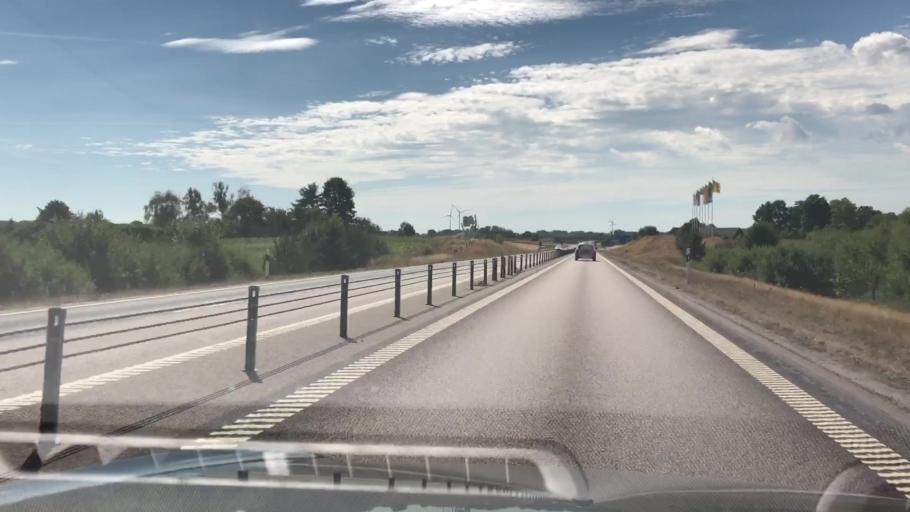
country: SE
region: Kalmar
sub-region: Torsas Kommun
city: Torsas
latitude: 56.4580
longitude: 16.0786
